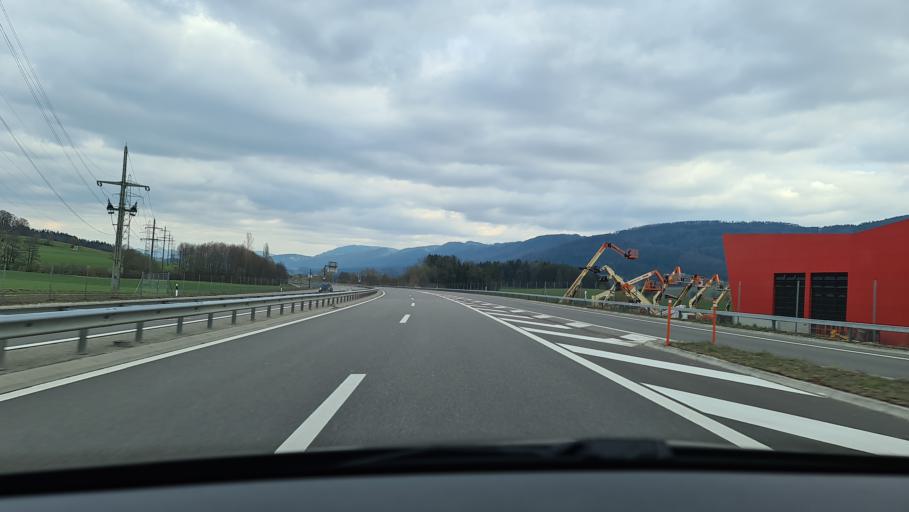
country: CH
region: Jura
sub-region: Delemont District
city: Glovelier
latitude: 47.3418
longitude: 7.2121
